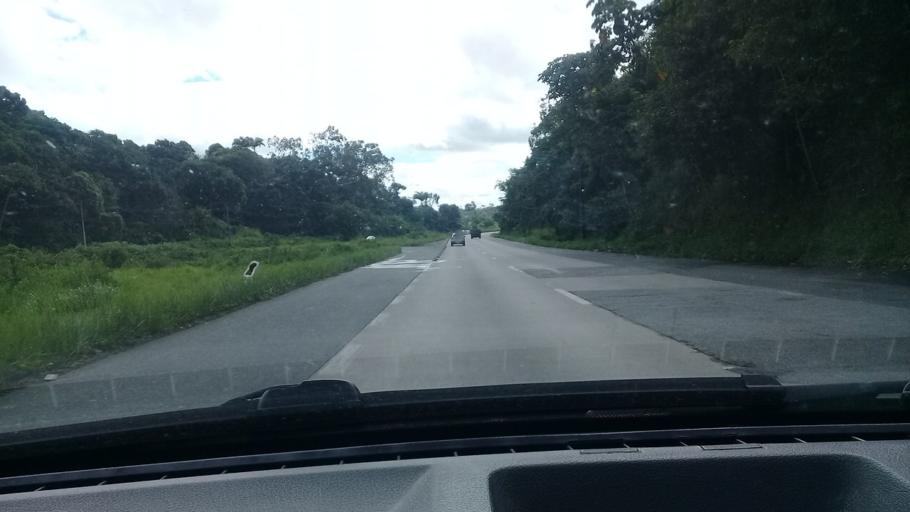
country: BR
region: Pernambuco
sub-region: Moreno
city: Moreno
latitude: -8.1055
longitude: -35.1033
